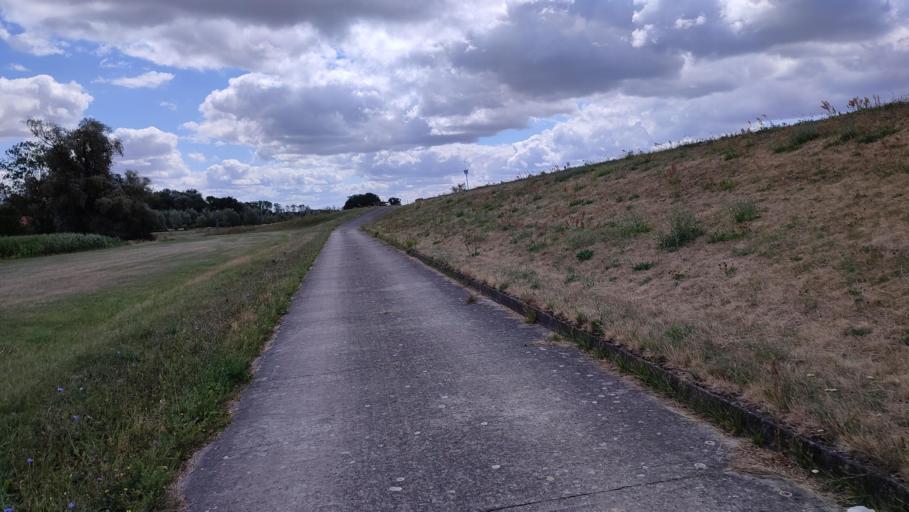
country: DE
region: Lower Saxony
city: Hitzacker
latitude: 53.2024
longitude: 10.9745
